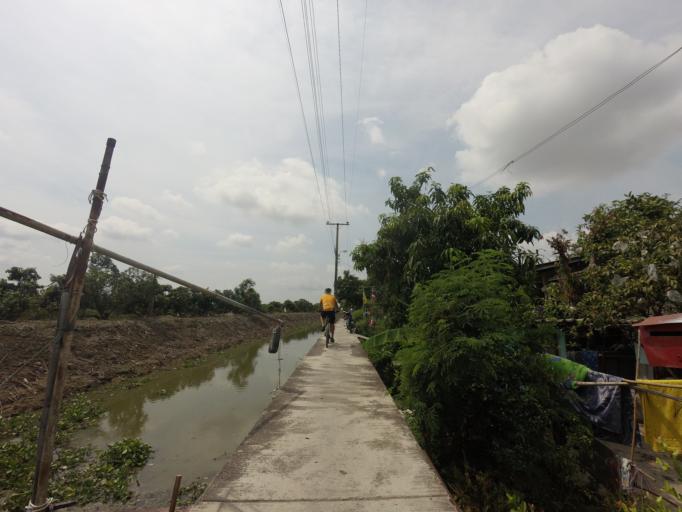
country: TH
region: Bangkok
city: Lat Krabang
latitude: 13.6612
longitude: 100.7642
